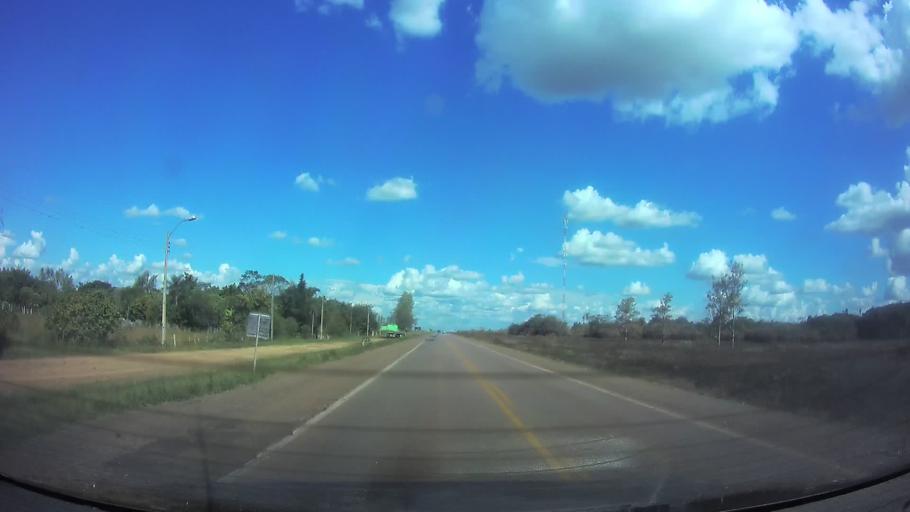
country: PY
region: Paraguari
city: Sapucai
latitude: -25.6950
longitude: -56.8582
